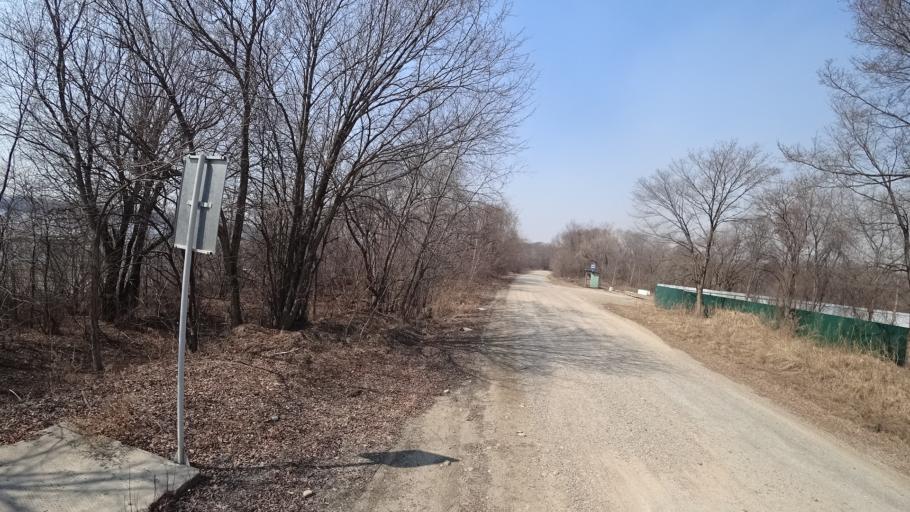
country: RU
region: Amur
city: Novobureyskiy
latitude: 49.7880
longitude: 129.9100
